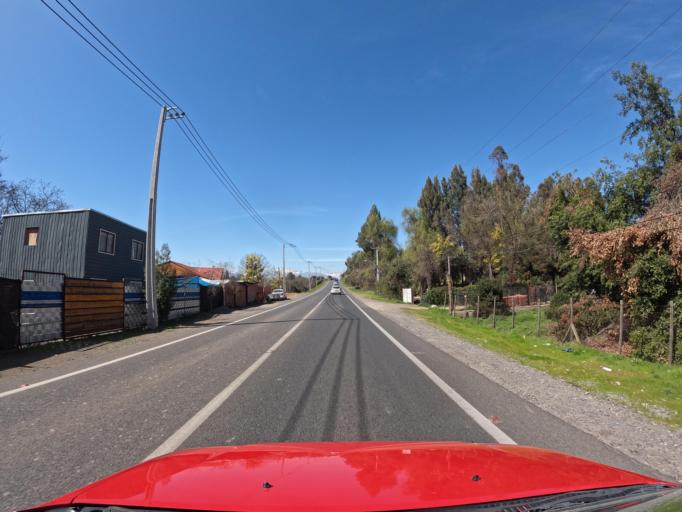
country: CL
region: Maule
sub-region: Provincia de Curico
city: Teno
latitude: -34.9629
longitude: -71.0750
